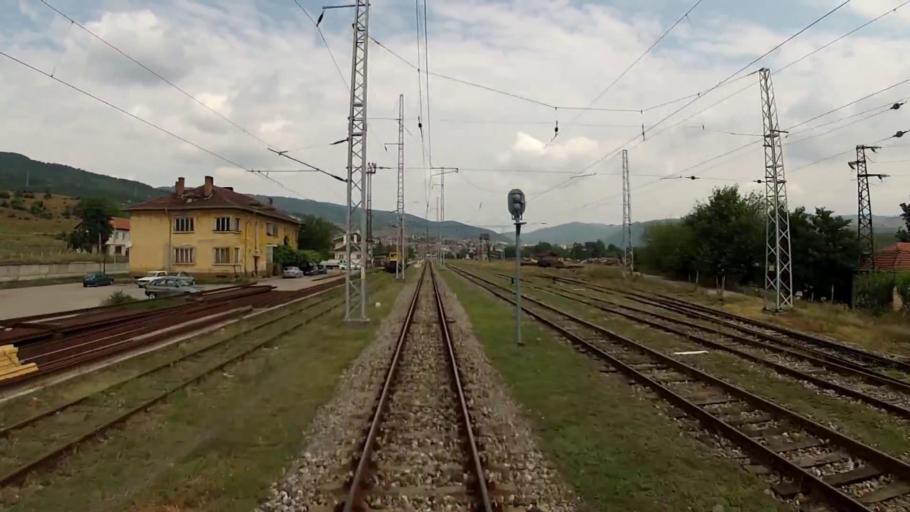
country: BG
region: Blagoevgrad
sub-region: Obshtina Simitli
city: Simitli
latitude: 41.8775
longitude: 23.1111
